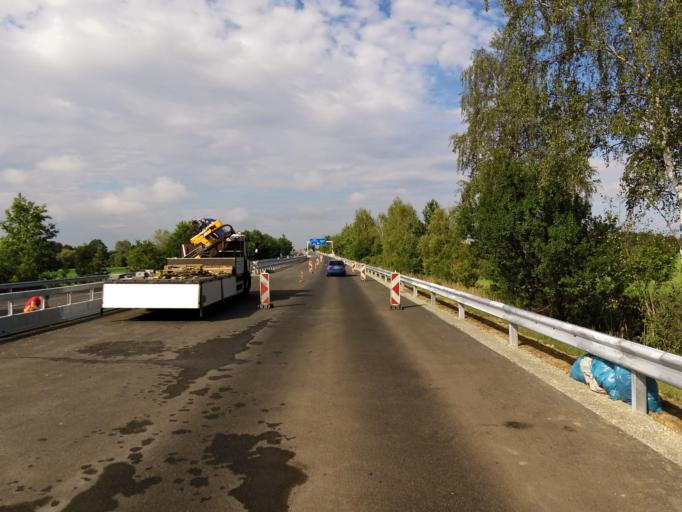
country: CZ
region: Jihocesky
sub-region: Okres Jindrichuv Hradec
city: Trebon
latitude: 49.0117
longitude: 14.7716
